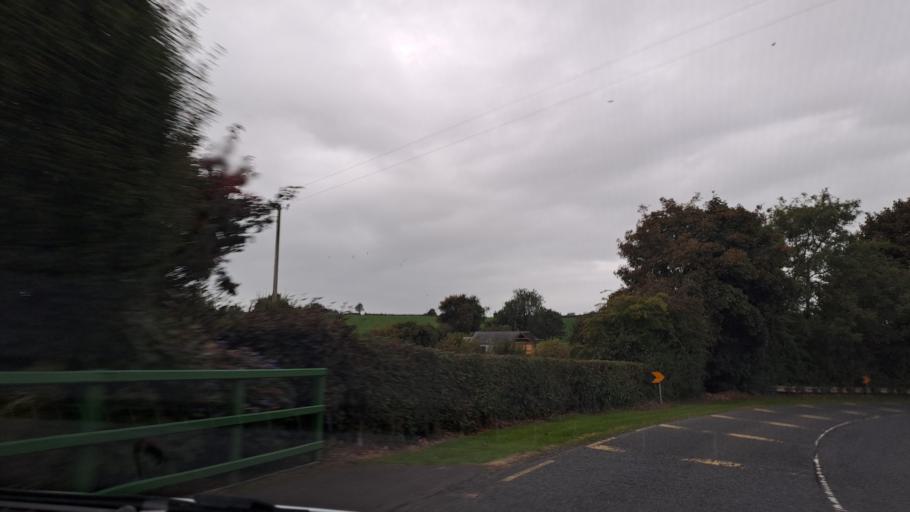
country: IE
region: Ulster
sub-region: County Monaghan
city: Monaghan
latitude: 54.2245
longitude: -6.9544
